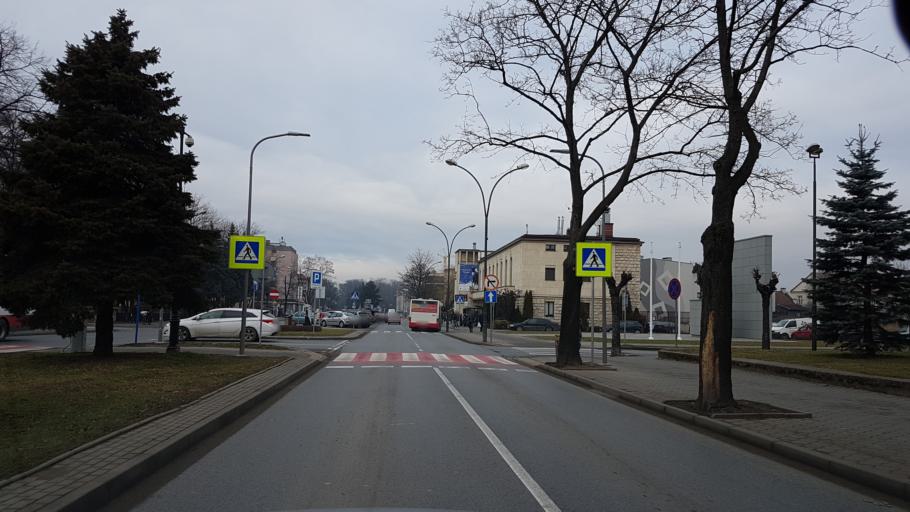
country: PL
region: Lesser Poland Voivodeship
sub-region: Powiat nowosadecki
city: Nowy Sacz
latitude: 49.6153
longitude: 20.6978
